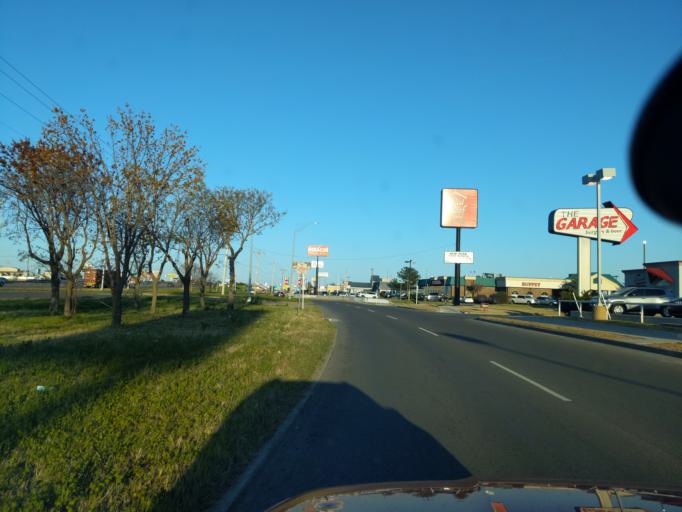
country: US
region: Oklahoma
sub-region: Cleveland County
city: Moore
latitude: 35.3909
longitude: -97.5341
